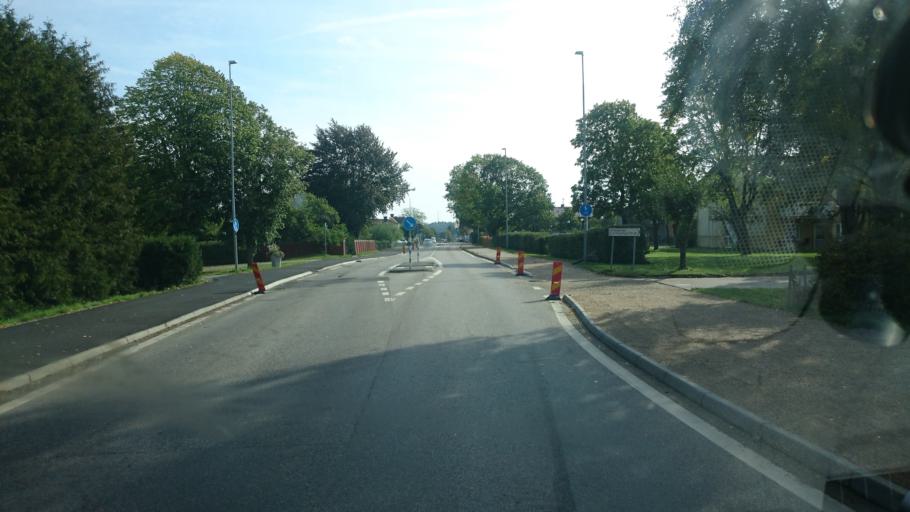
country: SE
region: Vaestra Goetaland
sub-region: Alingsas Kommun
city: Sollebrunn
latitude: 58.1215
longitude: 12.5279
